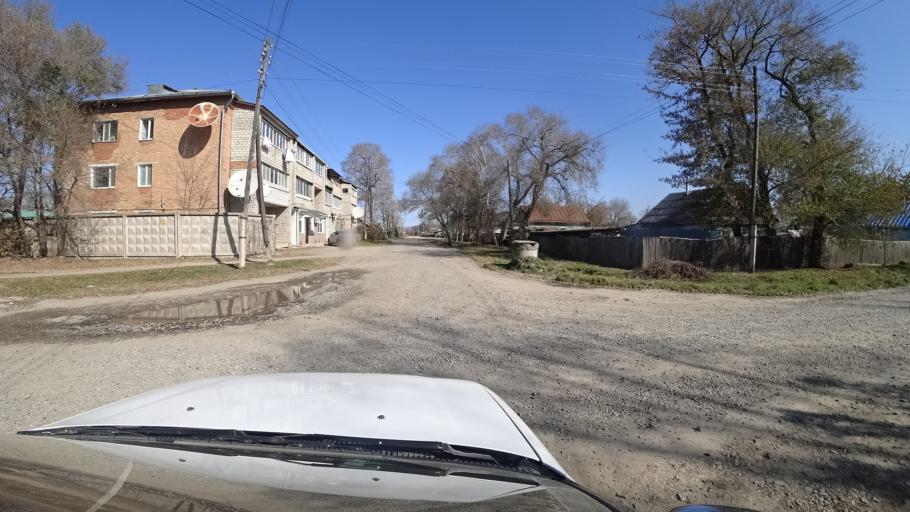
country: RU
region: Primorskiy
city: Dal'nerechensk
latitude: 45.9311
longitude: 133.7454
